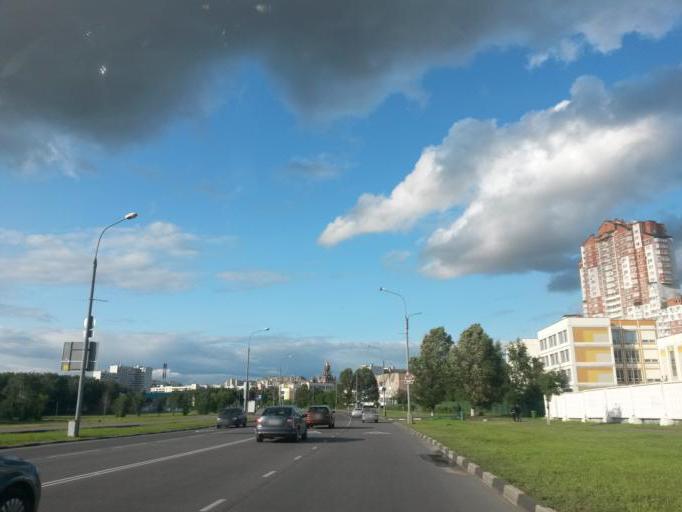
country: RU
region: Moscow
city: Zhulebino
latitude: 55.6886
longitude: 37.8479
